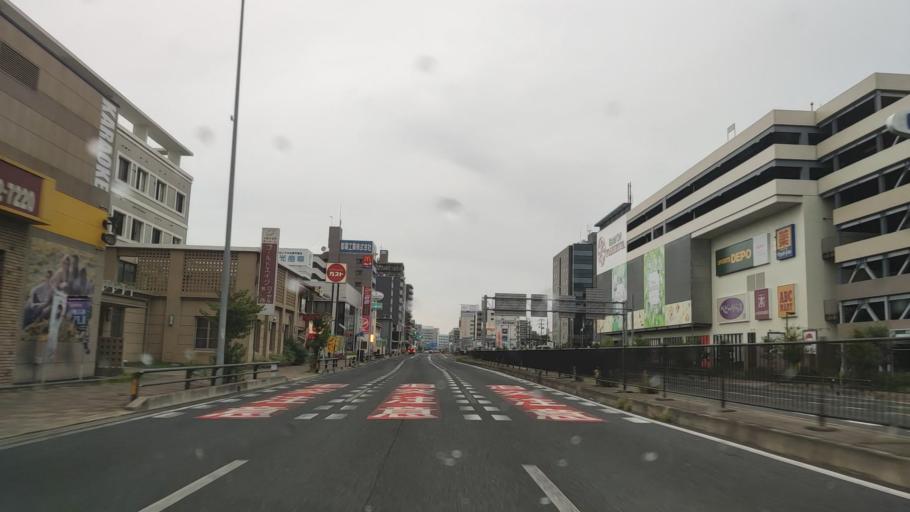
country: JP
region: Aichi
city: Nagoya-shi
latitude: 35.1900
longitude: 136.8770
